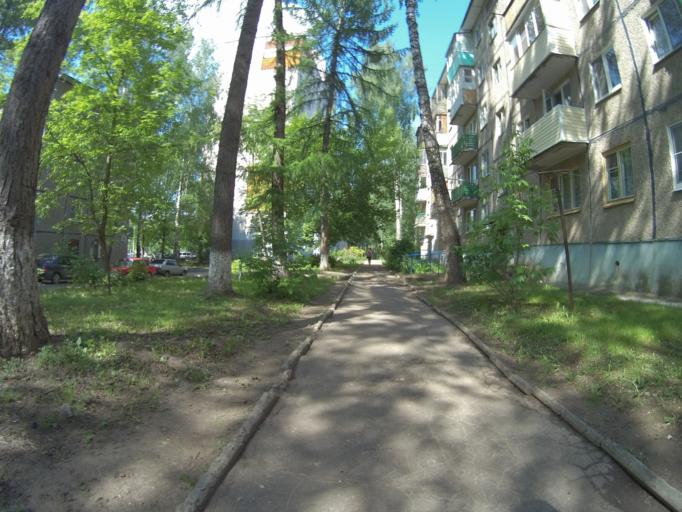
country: RU
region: Vladimir
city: Vladimir
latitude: 56.1320
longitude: 40.3547
